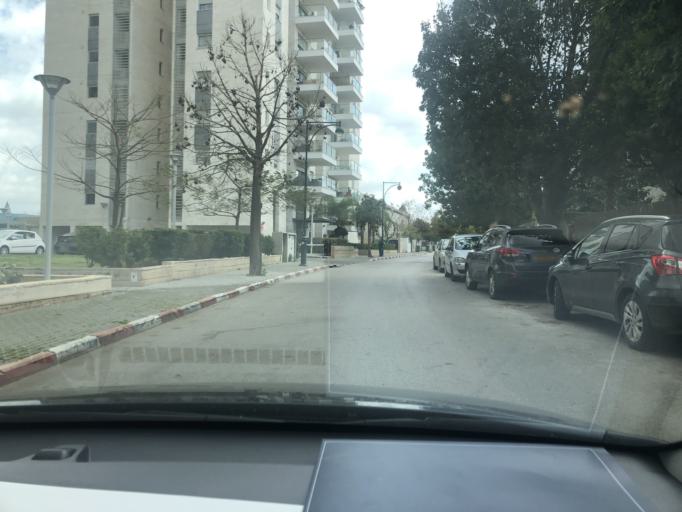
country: IL
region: Haifa
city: Hadera
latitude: 32.4671
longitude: 34.9548
